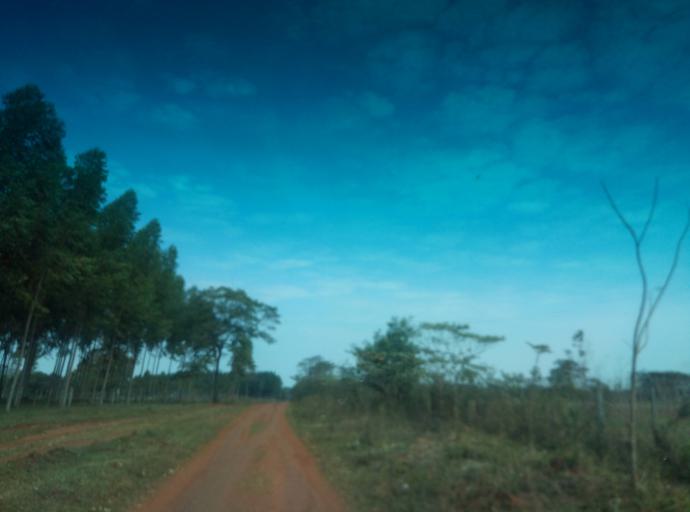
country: PY
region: Caaguazu
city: Carayao
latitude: -25.1913
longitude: -56.2520
